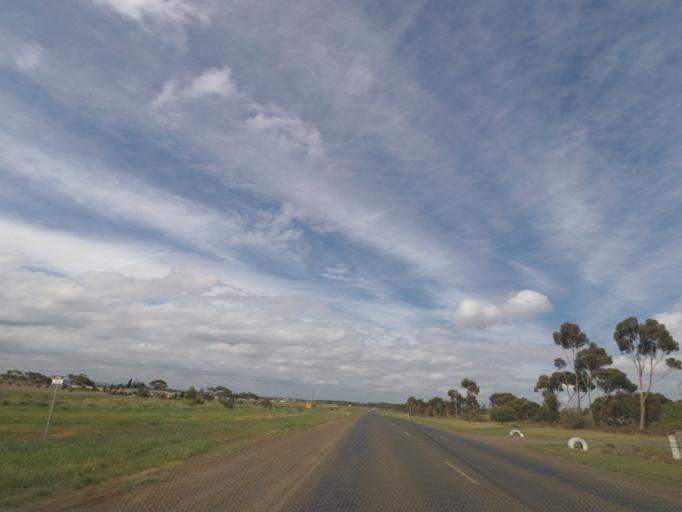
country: AU
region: Victoria
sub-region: Melton
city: Rockbank
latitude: -37.7446
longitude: 144.6548
